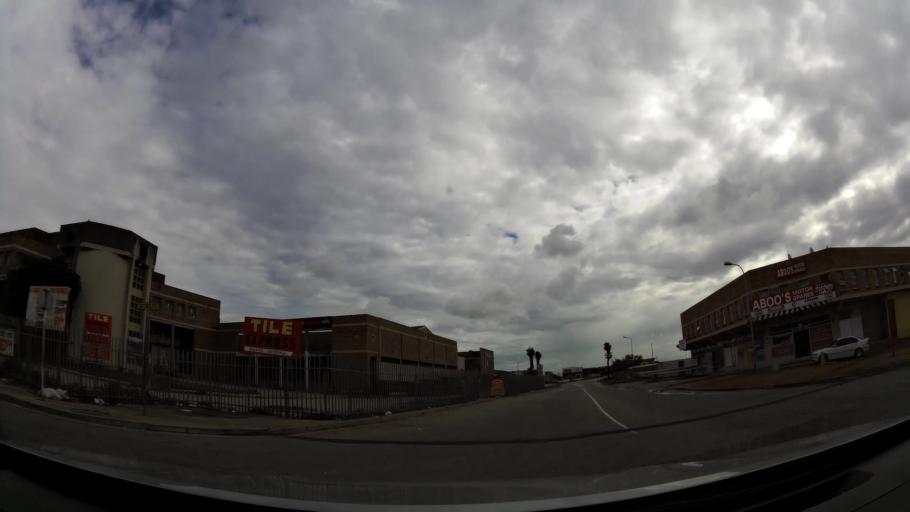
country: ZA
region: Eastern Cape
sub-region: Nelson Mandela Bay Metropolitan Municipality
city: Port Elizabeth
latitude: -33.9315
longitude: 25.5857
